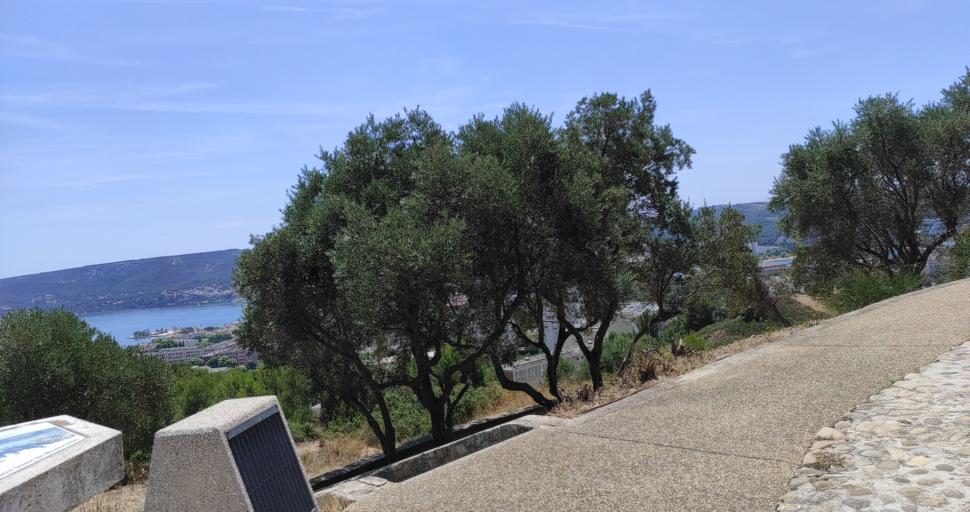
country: FR
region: Provence-Alpes-Cote d'Azur
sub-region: Departement des Bouches-du-Rhone
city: Martigues
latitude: 43.4158
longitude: 5.0465
